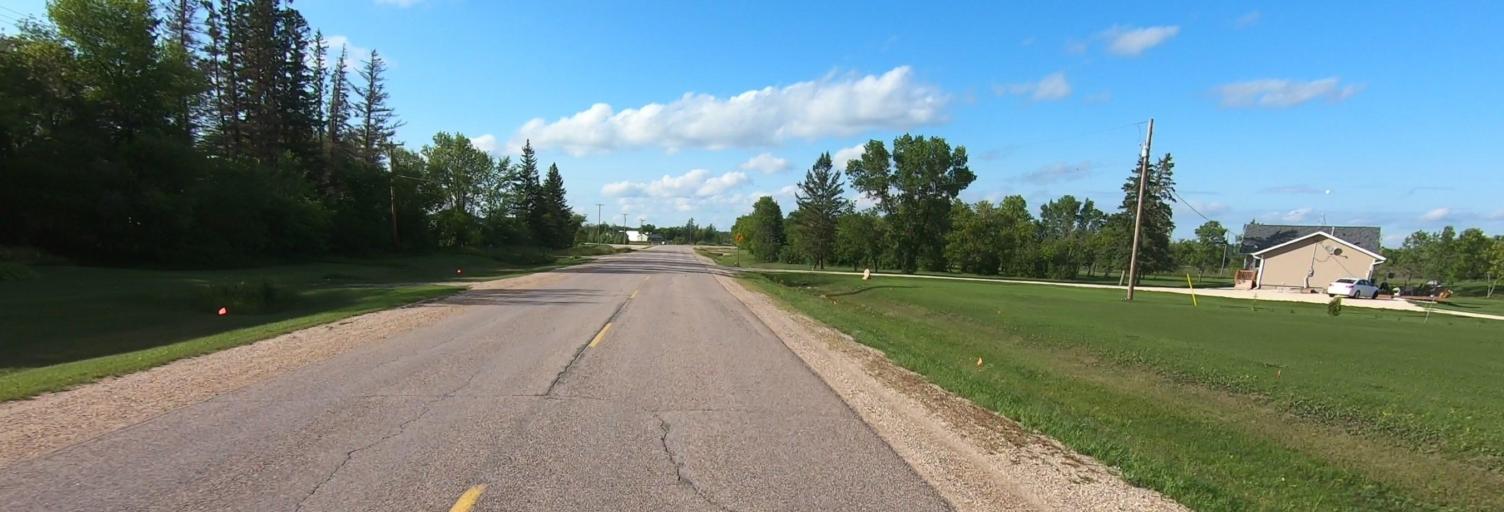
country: CA
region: Manitoba
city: Selkirk
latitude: 50.2091
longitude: -96.8407
